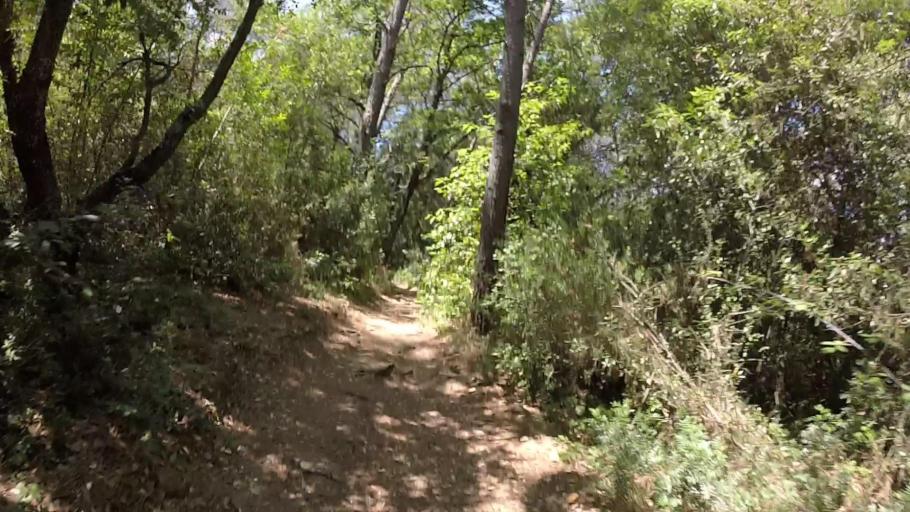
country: FR
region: Provence-Alpes-Cote d'Azur
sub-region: Departement des Alpes-Maritimes
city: Le Cannet
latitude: 43.5971
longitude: 7.0292
